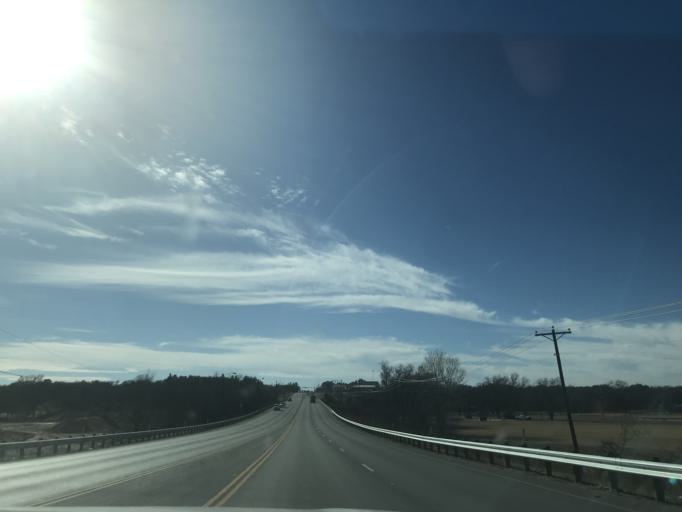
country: US
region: Texas
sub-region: Erath County
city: Stephenville
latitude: 32.2103
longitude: -98.1989
